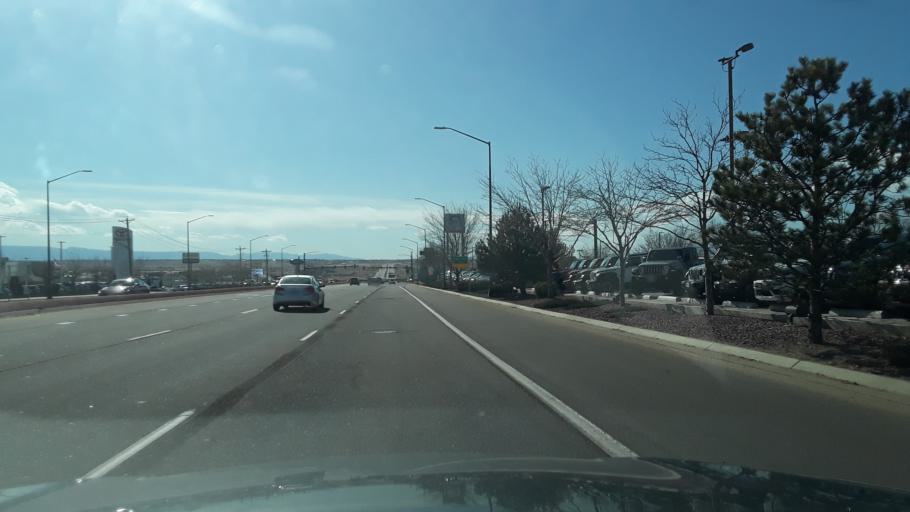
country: US
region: Colorado
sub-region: Pueblo County
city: Pueblo
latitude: 38.3109
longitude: -104.6384
